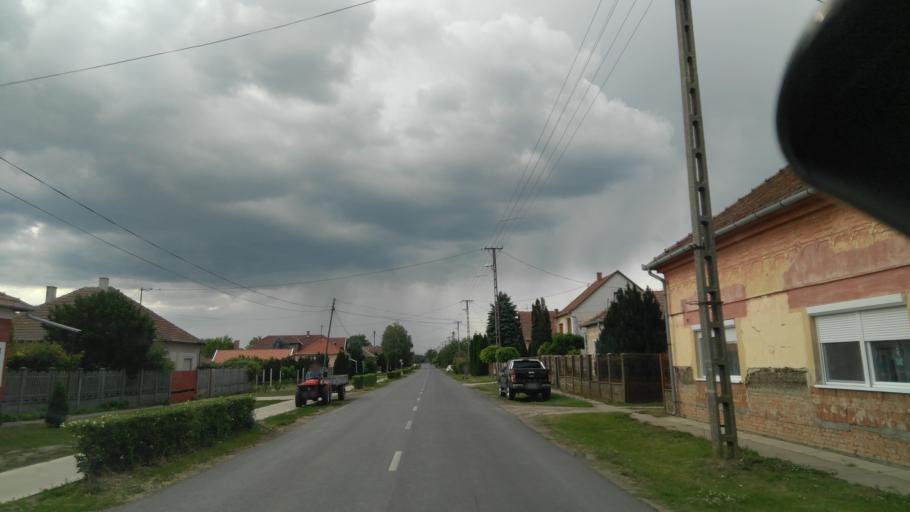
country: HU
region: Bekes
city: Dombegyhaz
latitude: 46.3419
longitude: 21.1287
